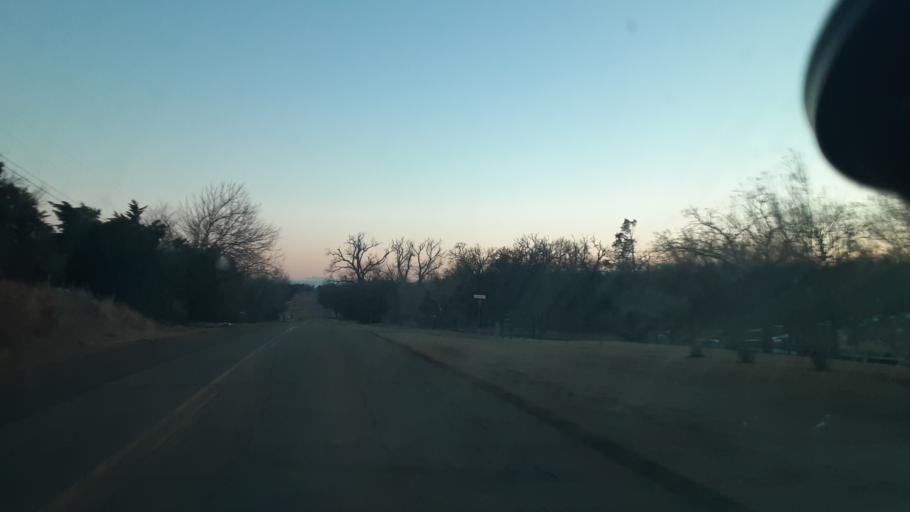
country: US
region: Oklahoma
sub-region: Oklahoma County
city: Edmond
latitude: 35.7202
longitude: -97.4252
